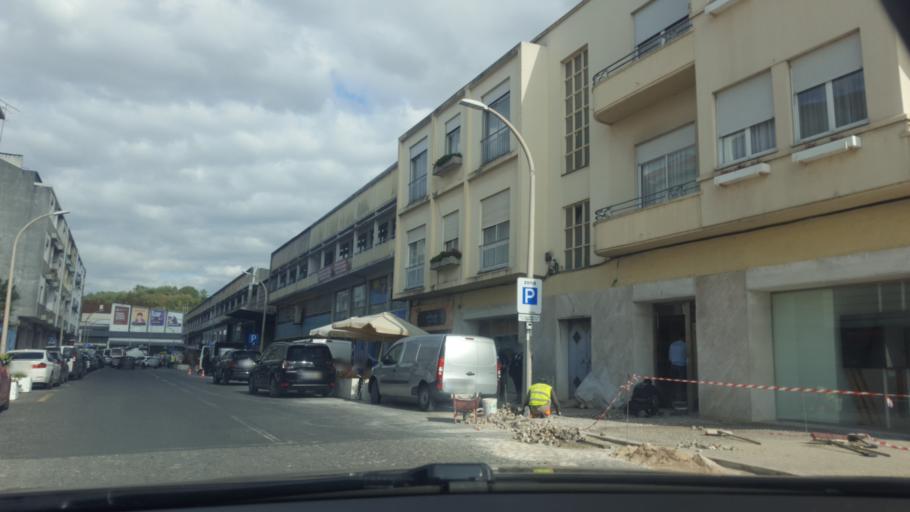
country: PT
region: Leiria
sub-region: Leiria
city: Leiria
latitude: 39.7452
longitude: -8.8057
